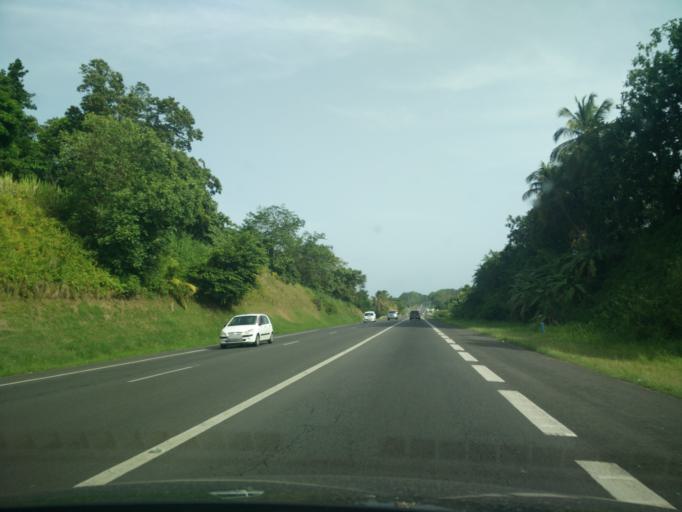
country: GP
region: Guadeloupe
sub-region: Guadeloupe
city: Petit-Bourg
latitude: 16.1535
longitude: -61.5850
